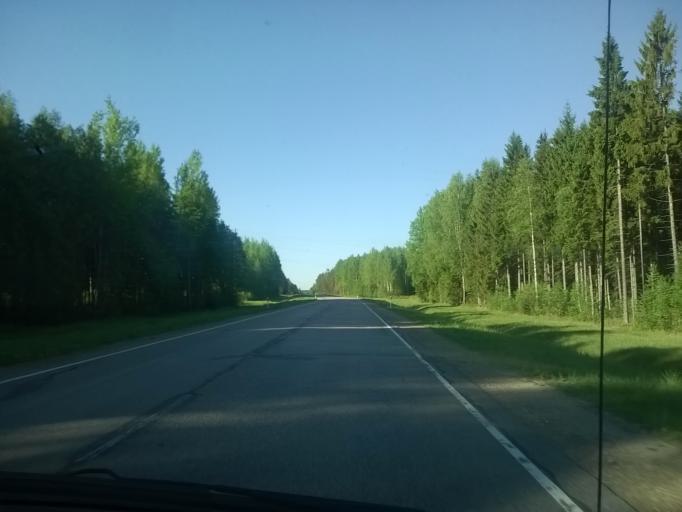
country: EE
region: Valgamaa
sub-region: Valga linn
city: Valga
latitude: 57.8692
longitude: 26.1490
